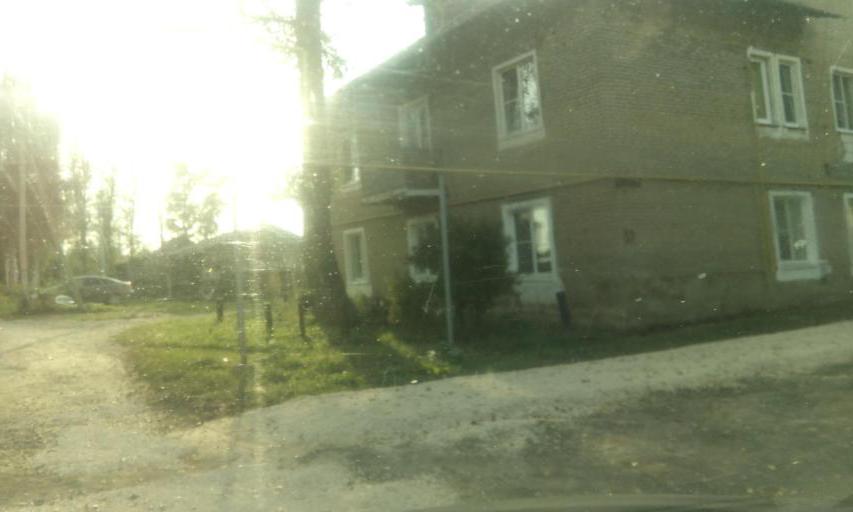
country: RU
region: Tula
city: Partizan
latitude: 53.9467
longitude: 38.1001
